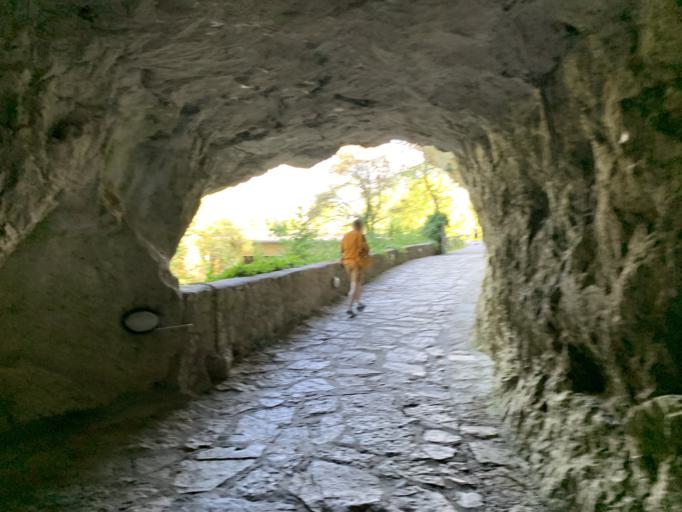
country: ES
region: Asturias
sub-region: Province of Asturias
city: Carrena
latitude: 43.2989
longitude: -4.8195
